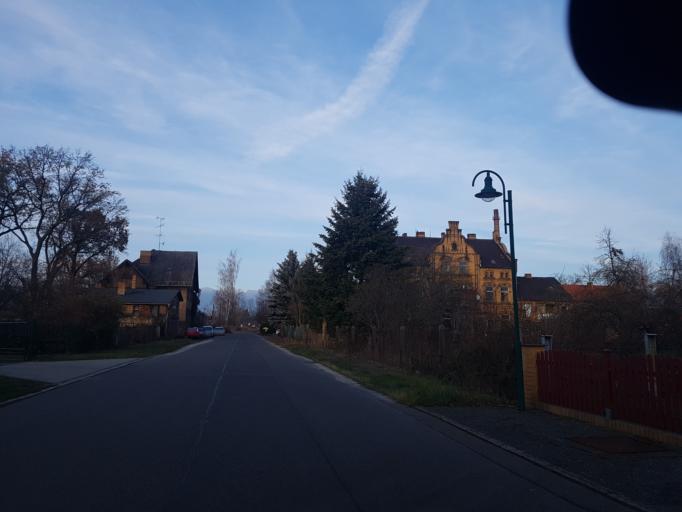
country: DE
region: Brandenburg
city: Finsterwalde
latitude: 51.6386
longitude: 13.7188
